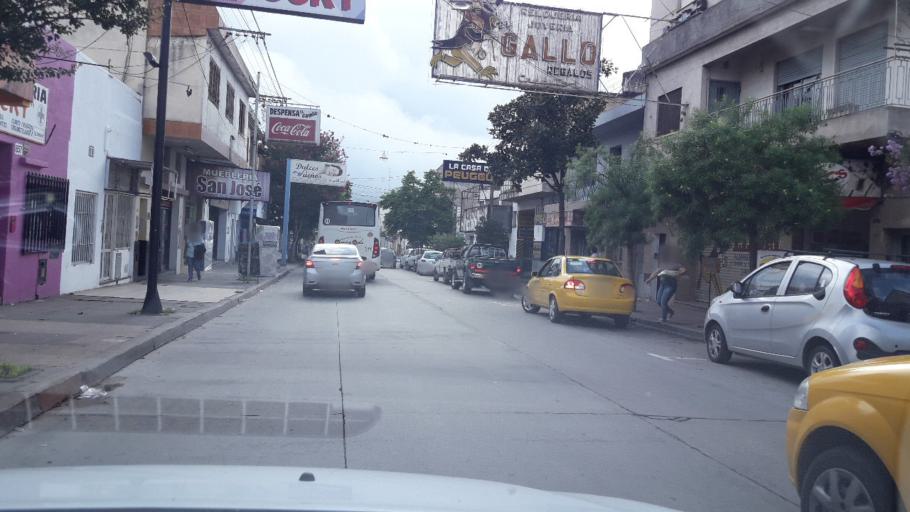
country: AR
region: Jujuy
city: San Salvador de Jujuy
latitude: -24.1911
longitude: -65.3008
